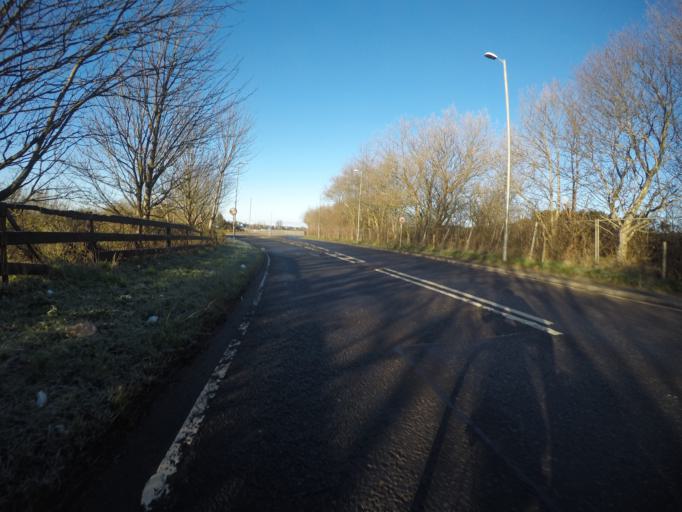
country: GB
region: Scotland
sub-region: North Ayrshire
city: Stevenston
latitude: 55.6351
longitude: -4.7428
